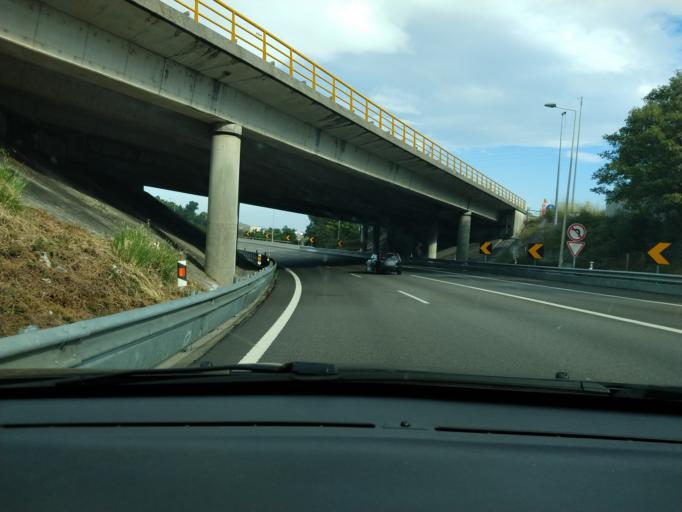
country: PT
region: Porto
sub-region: Vila Nova de Gaia
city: Perozinho
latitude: 41.0761
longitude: -8.5784
